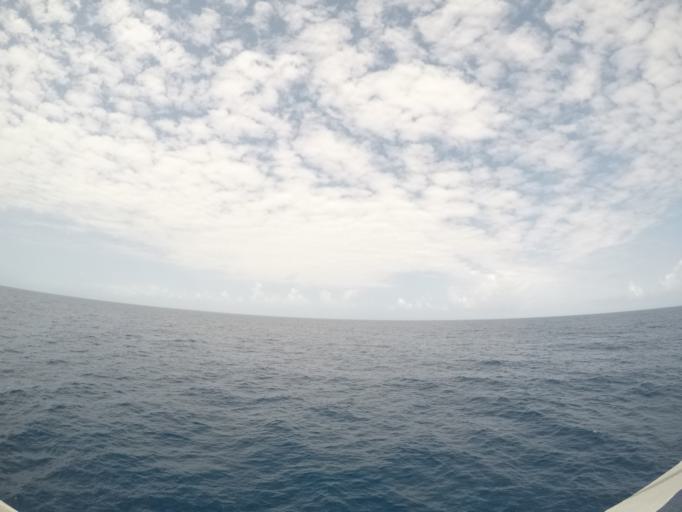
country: TZ
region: Zanzibar North
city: Nungwi
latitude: -5.5898
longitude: 39.3502
